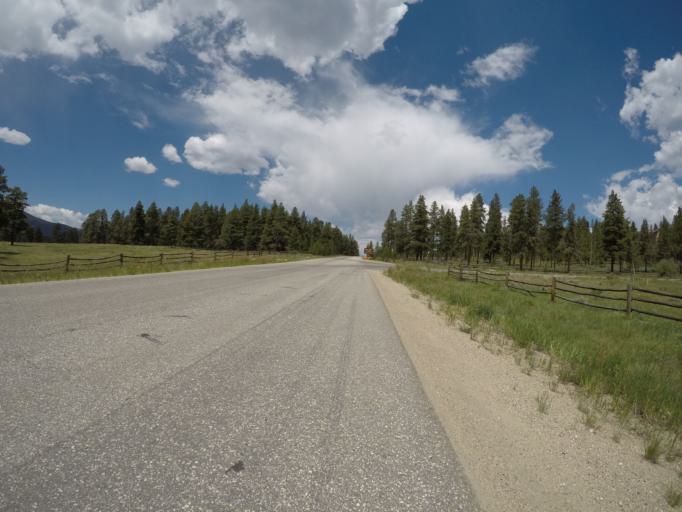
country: US
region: Colorado
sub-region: Grand County
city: Fraser
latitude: 39.9849
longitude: -105.8769
